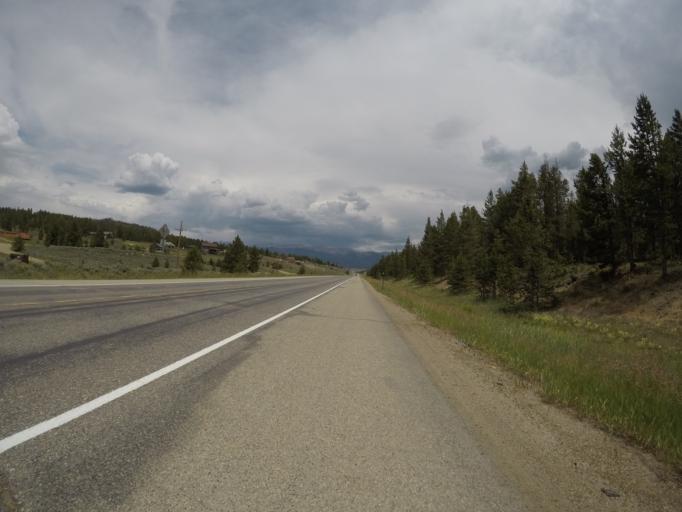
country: US
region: Colorado
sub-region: Grand County
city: Fraser
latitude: 39.9972
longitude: -105.8916
